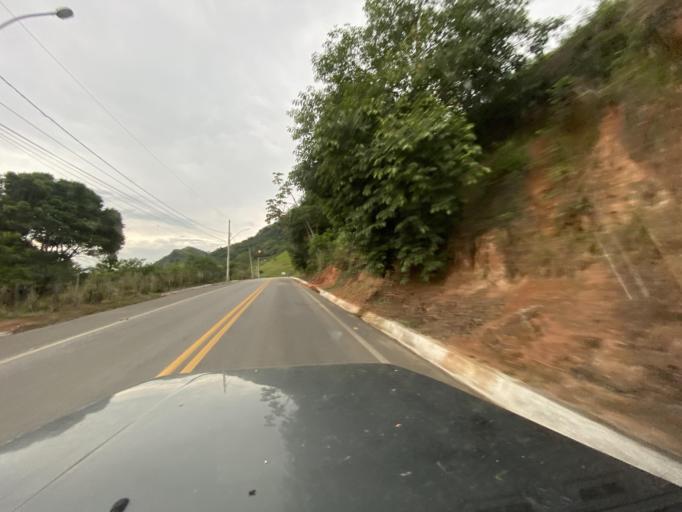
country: BR
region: Espirito Santo
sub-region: Jeronimo Monteiro
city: Jeronimo Monteiro
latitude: -20.8027
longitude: -41.3553
